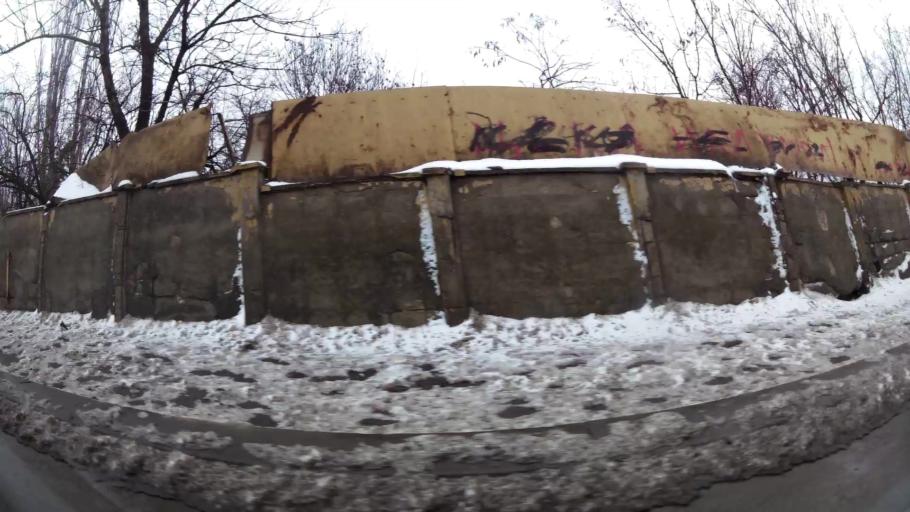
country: BG
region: Sofia-Capital
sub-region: Stolichna Obshtina
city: Sofia
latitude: 42.7148
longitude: 23.3393
